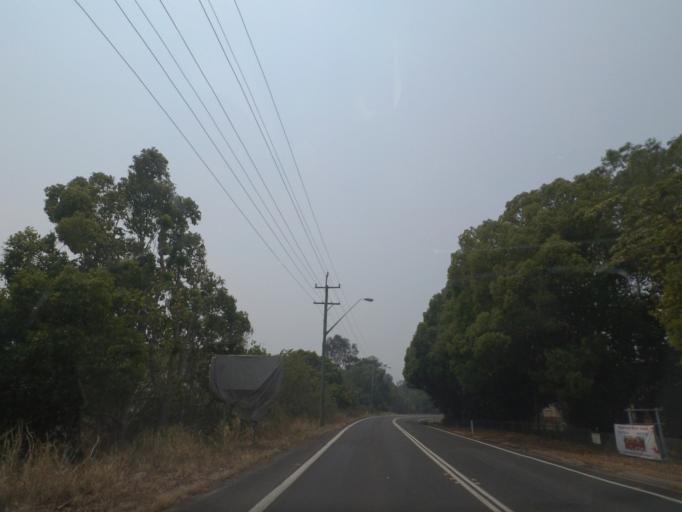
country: AU
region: New South Wales
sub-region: Richmond Valley
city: Evans Head
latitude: -29.0032
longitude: 153.4366
